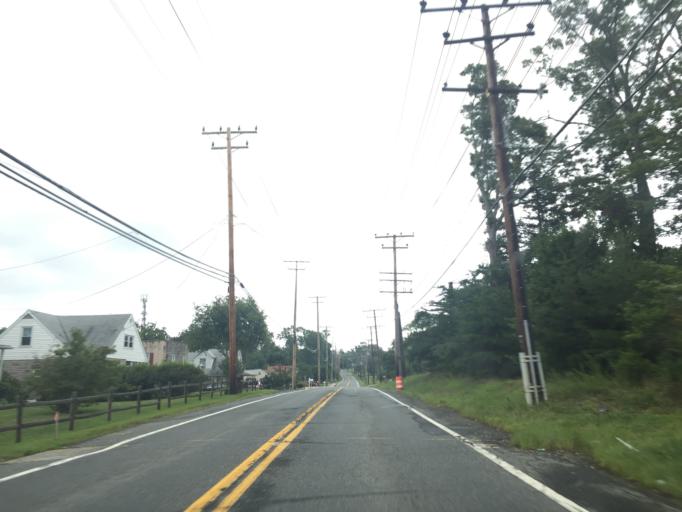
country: US
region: Maryland
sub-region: Harford County
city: Edgewood
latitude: 39.4560
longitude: -76.2844
